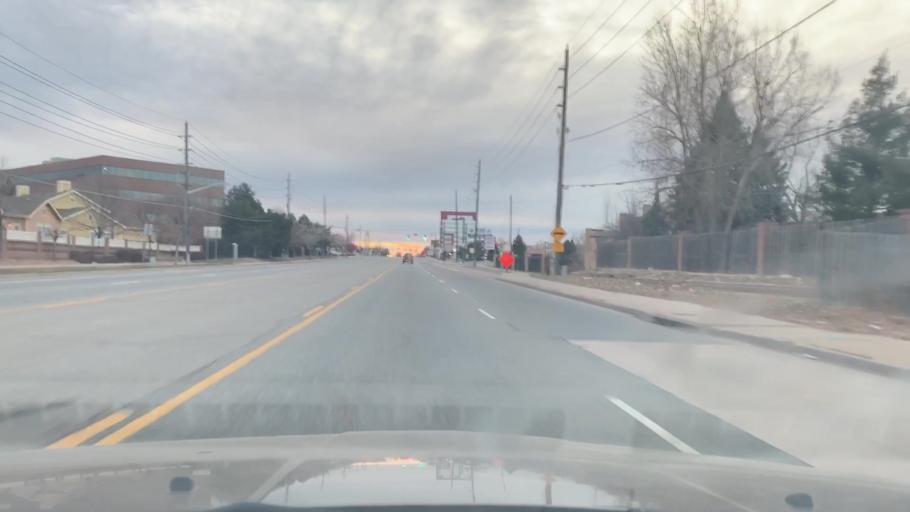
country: US
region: Colorado
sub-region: Arapahoe County
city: Glendale
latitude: 39.6782
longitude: -104.8752
